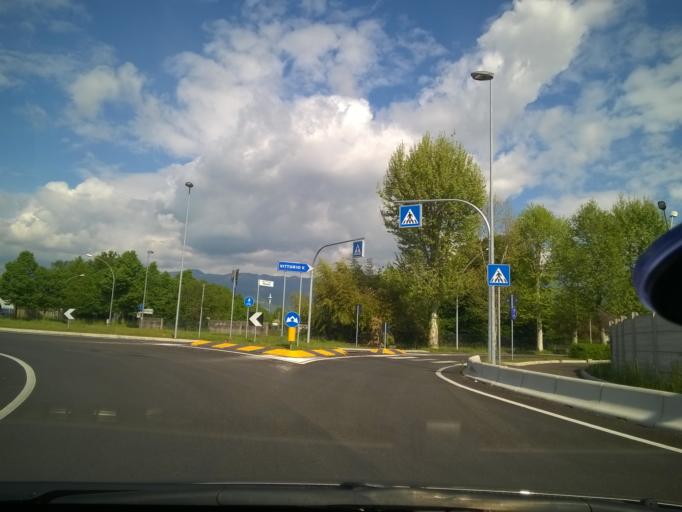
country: IT
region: Veneto
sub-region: Provincia di Treviso
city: Scomigo
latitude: 45.9476
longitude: 12.3235
